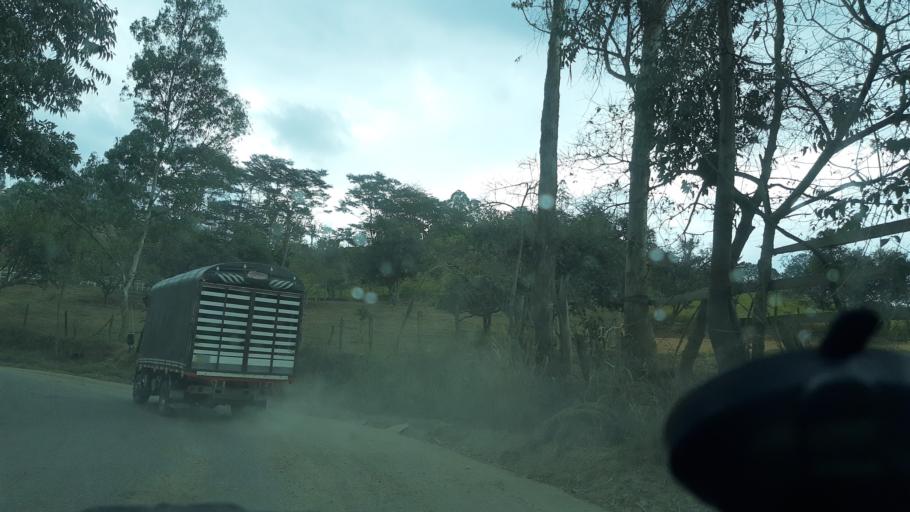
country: CO
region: Boyaca
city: Garagoa
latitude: 5.0756
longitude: -73.3738
